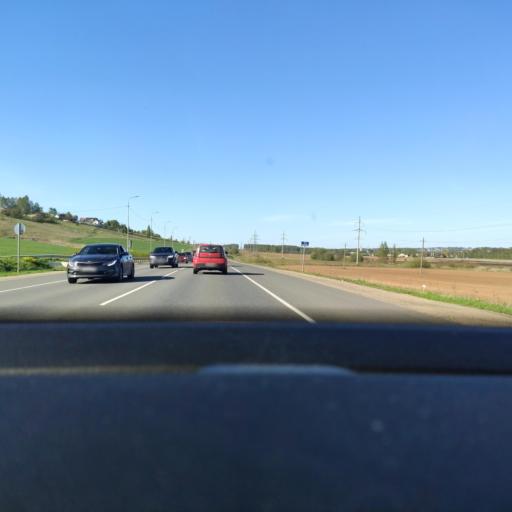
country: RU
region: Moskovskaya
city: Yakhroma
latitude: 56.3380
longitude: 37.4826
